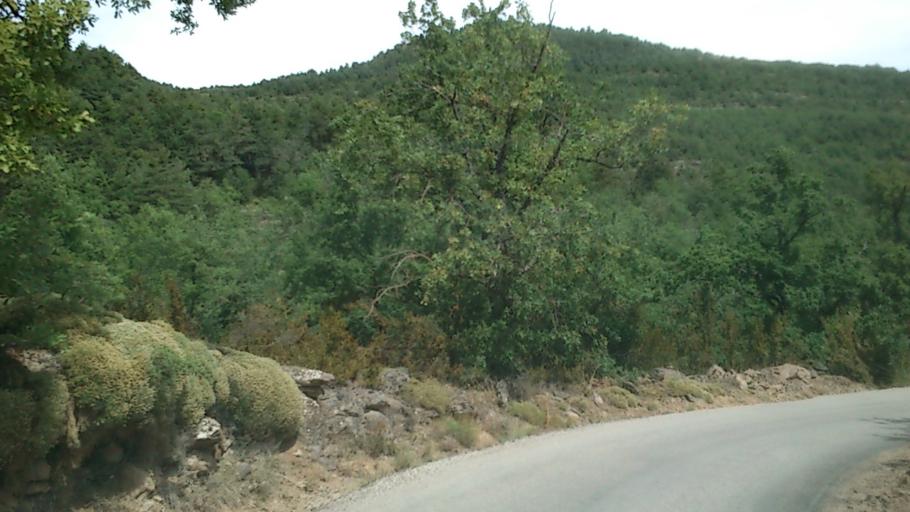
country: ES
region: Aragon
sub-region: Provincia de Huesca
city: Yebra de Basa
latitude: 42.3286
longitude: -0.2592
